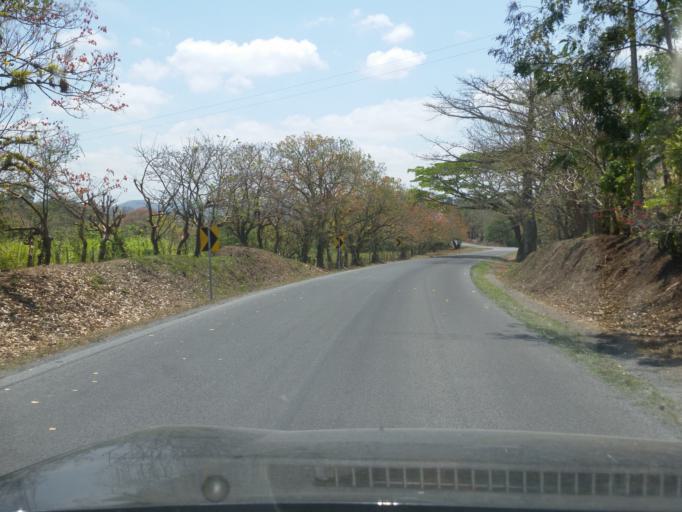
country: NI
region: Boaco
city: Boaco
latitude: 12.6021
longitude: -85.5401
